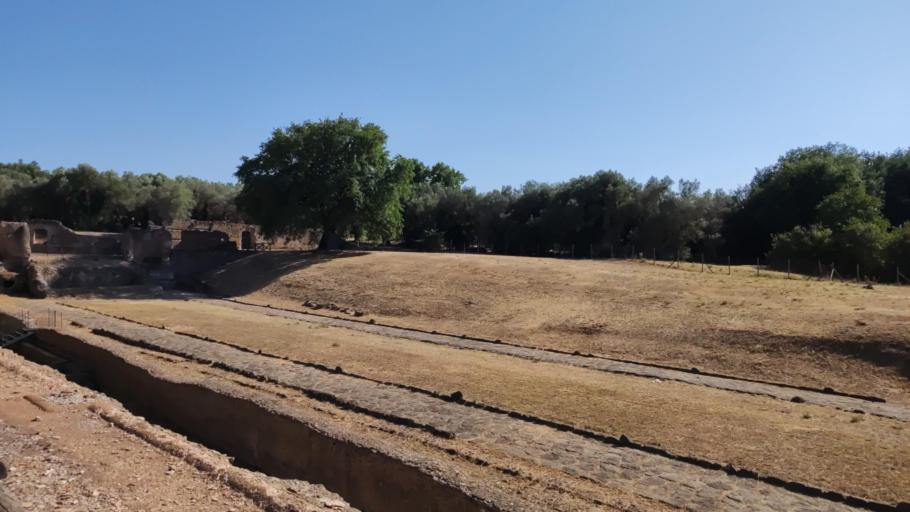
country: IT
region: Latium
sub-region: Citta metropolitana di Roma Capitale
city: Villa Adriana
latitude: 41.9408
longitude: 12.7744
